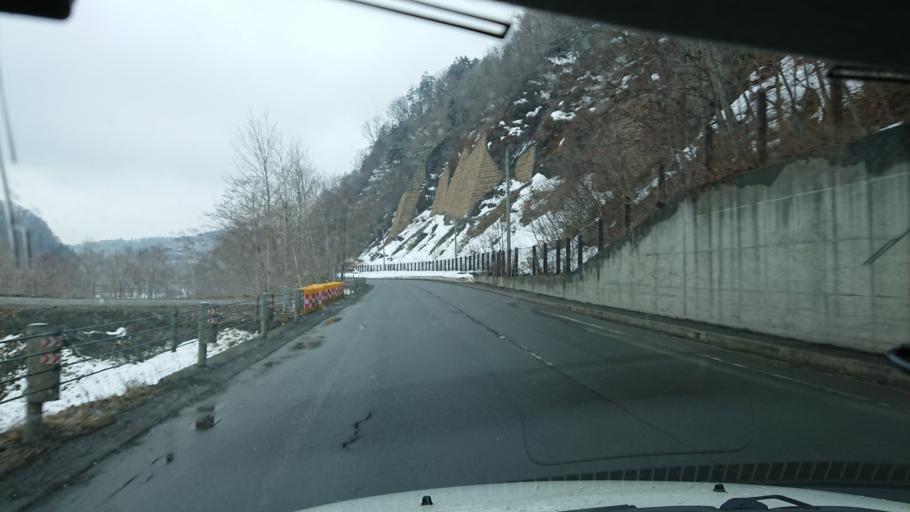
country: JP
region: Hokkaido
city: Kitahiroshima
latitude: 42.8472
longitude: 141.4368
